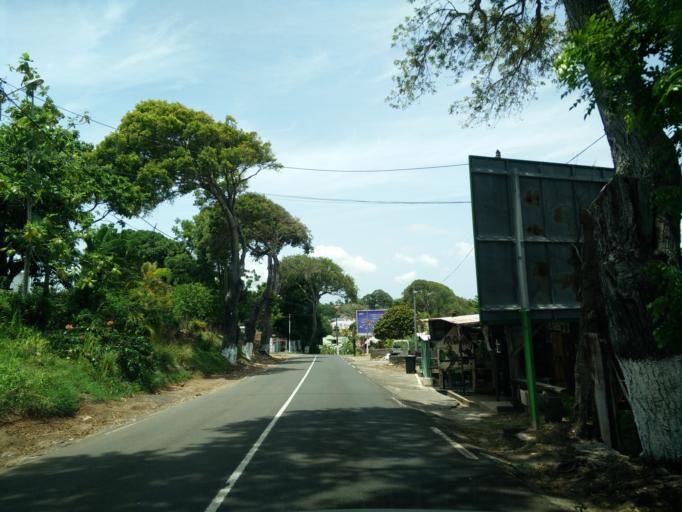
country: GP
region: Guadeloupe
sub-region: Guadeloupe
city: Petit-Bourg
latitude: 16.1849
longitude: -61.5891
